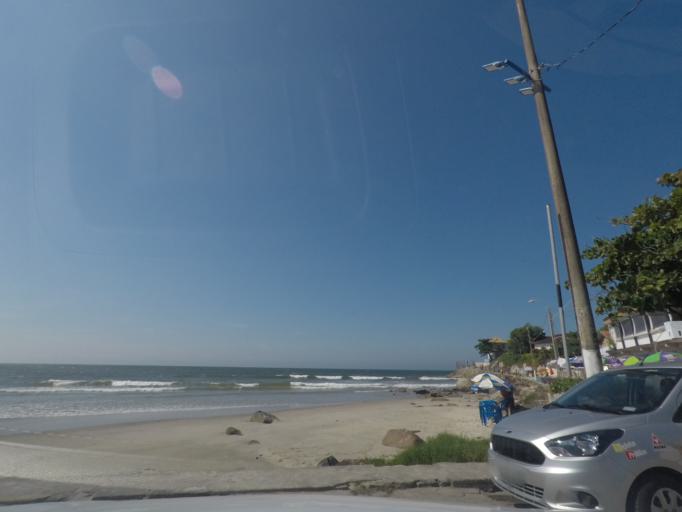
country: BR
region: Parana
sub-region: Guaratuba
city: Guaratuba
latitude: -25.8178
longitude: -48.5317
